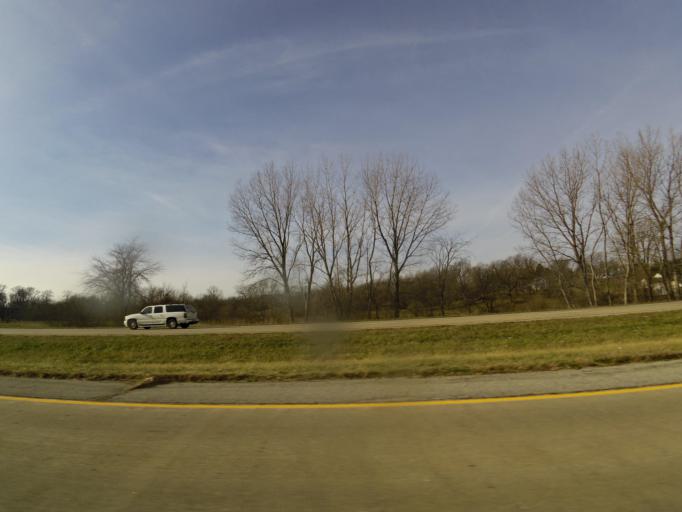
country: US
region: Illinois
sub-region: De Witt County
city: Clinton
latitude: 40.0984
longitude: -88.9654
